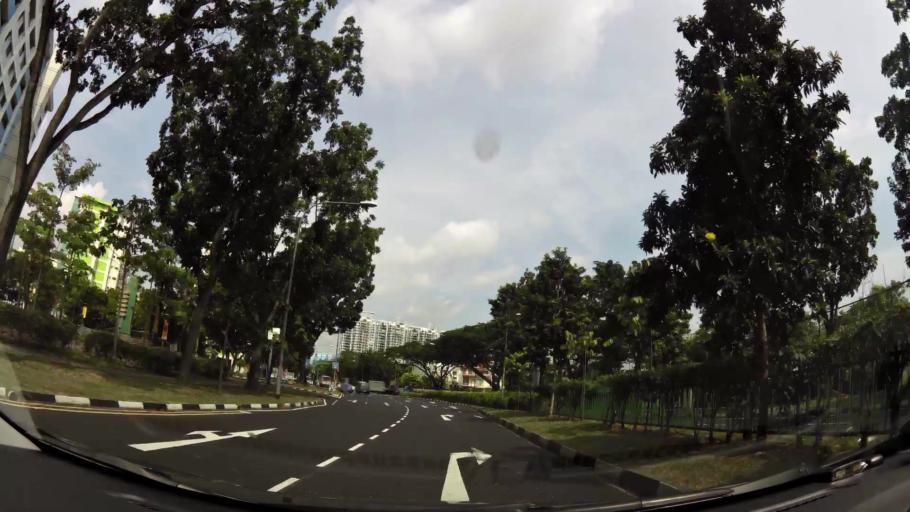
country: SG
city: Singapore
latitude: 1.3059
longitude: 103.7638
